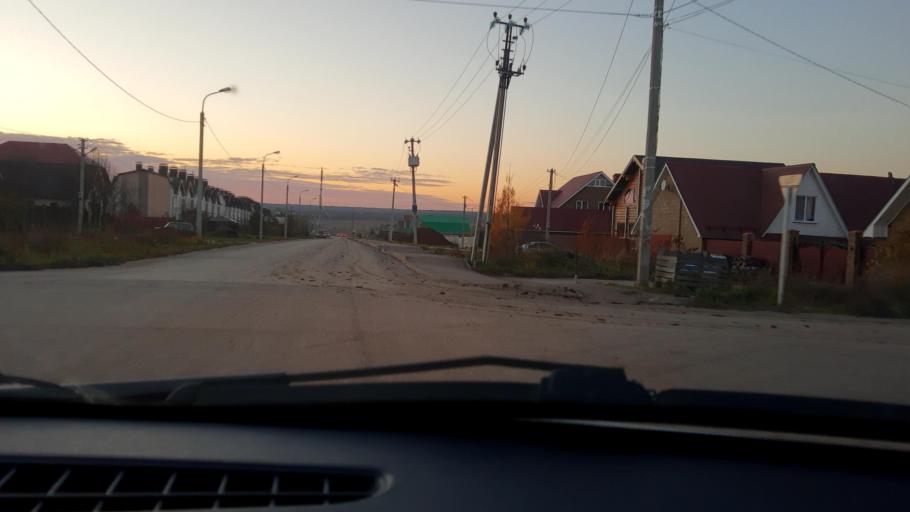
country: RU
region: Bashkortostan
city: Avdon
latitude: 54.6974
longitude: 55.8016
